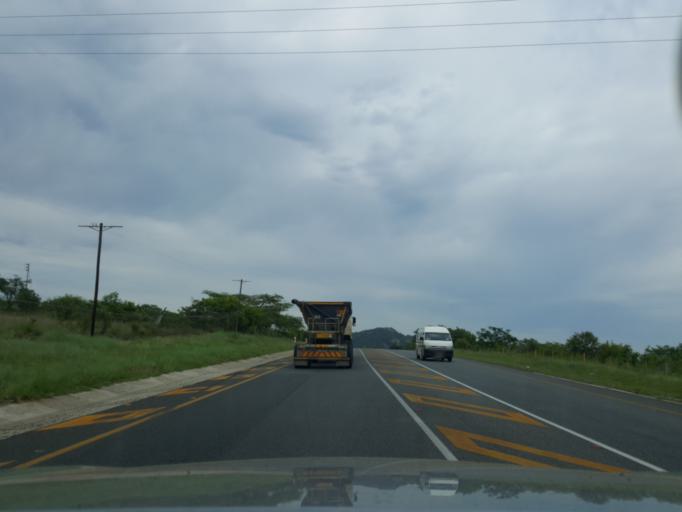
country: ZA
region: Mpumalanga
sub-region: Ehlanzeni District
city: Nelspruit
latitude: -25.4864
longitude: 31.1437
